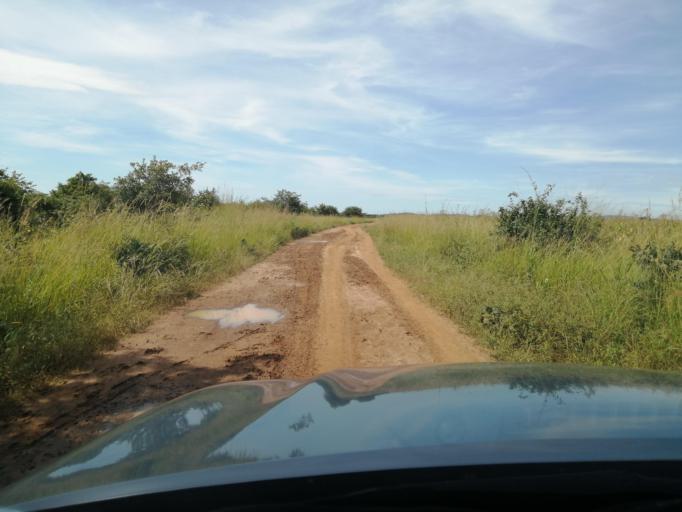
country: ZM
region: Central
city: Chibombo
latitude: -14.9648
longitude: 27.8056
